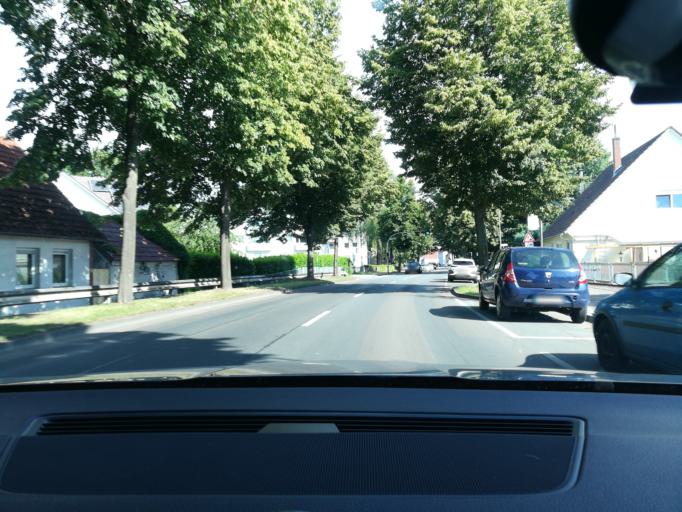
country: DE
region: North Rhine-Westphalia
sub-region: Regierungsbezirk Detmold
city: Minden
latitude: 52.3093
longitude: 8.8953
